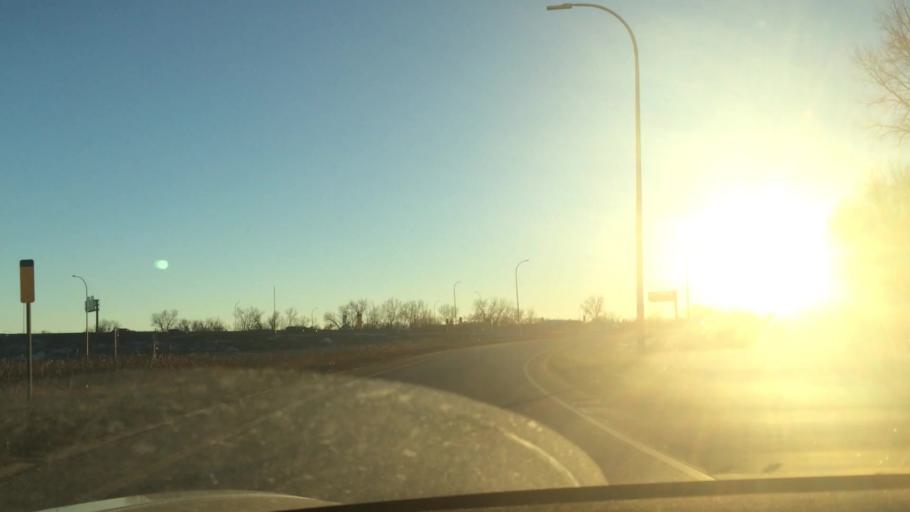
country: US
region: Minnesota
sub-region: Ramsey County
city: New Brighton
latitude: 45.0691
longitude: -93.1863
